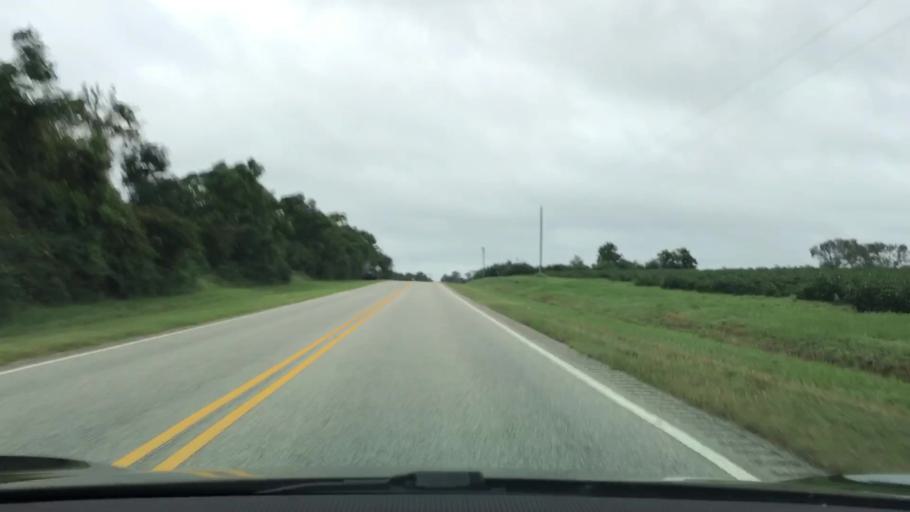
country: US
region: Alabama
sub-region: Coffee County
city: Elba
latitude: 31.3360
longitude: -86.1314
